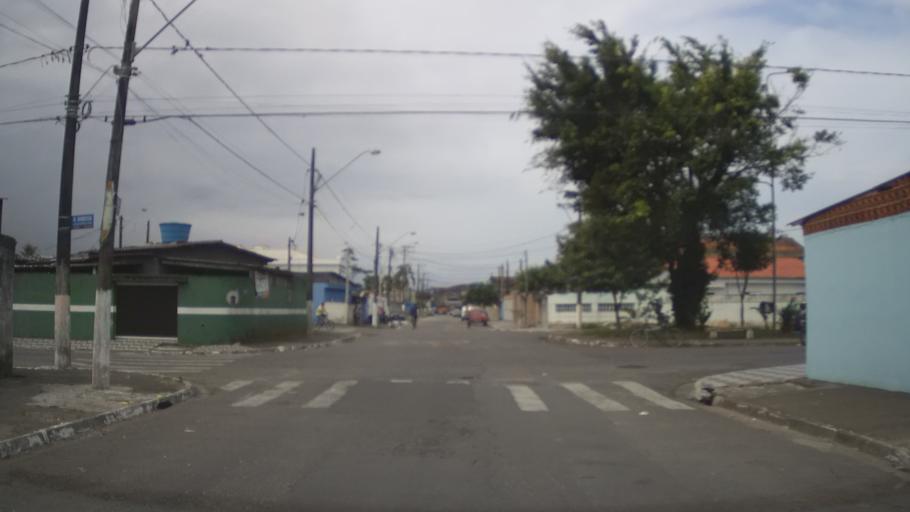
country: BR
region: Sao Paulo
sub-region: Praia Grande
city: Praia Grande
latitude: -24.0026
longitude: -46.4480
